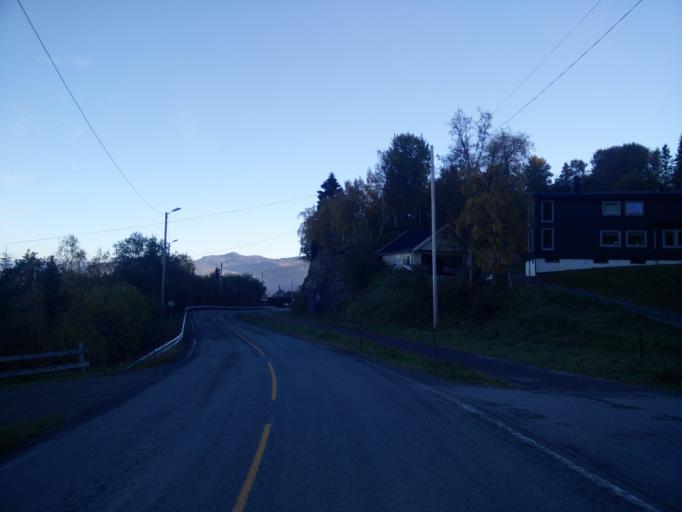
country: NO
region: Sor-Trondelag
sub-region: Skaun
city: Borsa
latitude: 63.3389
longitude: 10.0574
